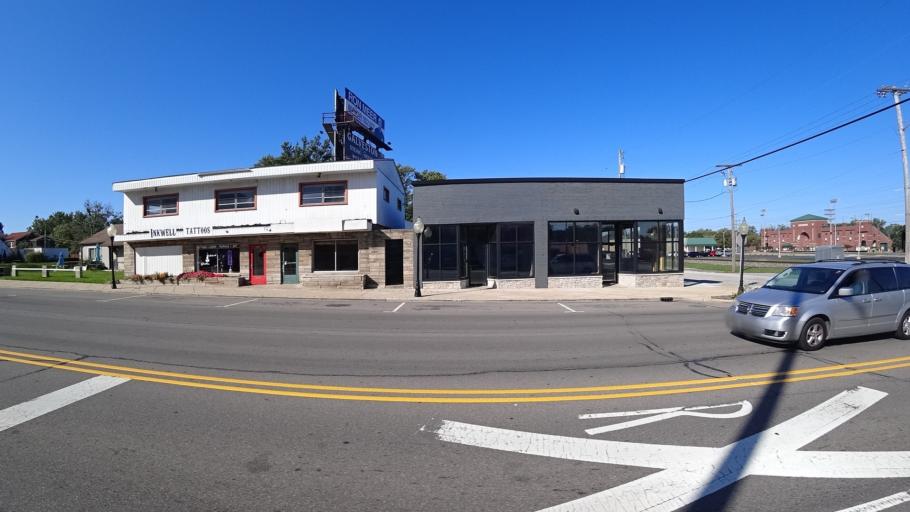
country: US
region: Indiana
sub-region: LaPorte County
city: Michigan City
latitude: 41.6999
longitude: -86.8942
